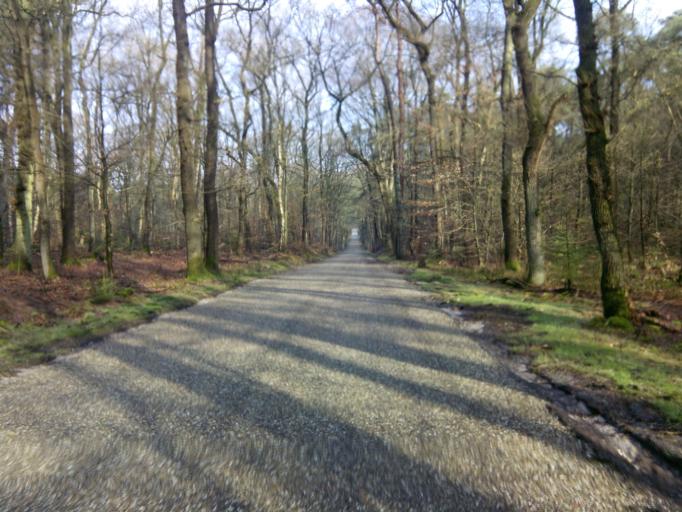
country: NL
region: Utrecht
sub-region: Gemeente Utrechtse Heuvelrug
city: Maarsbergen
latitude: 52.0398
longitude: 5.3976
